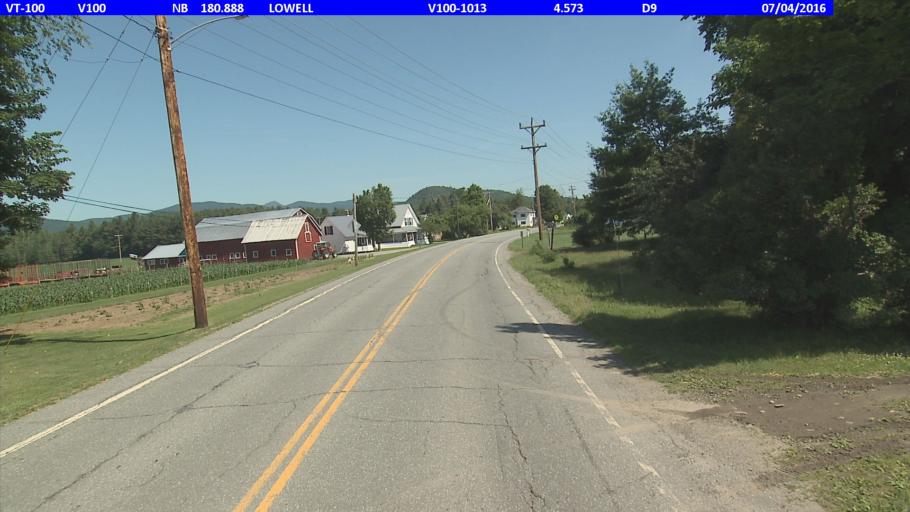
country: US
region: Vermont
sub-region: Lamoille County
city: Hyde Park
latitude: 44.8020
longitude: -72.4482
